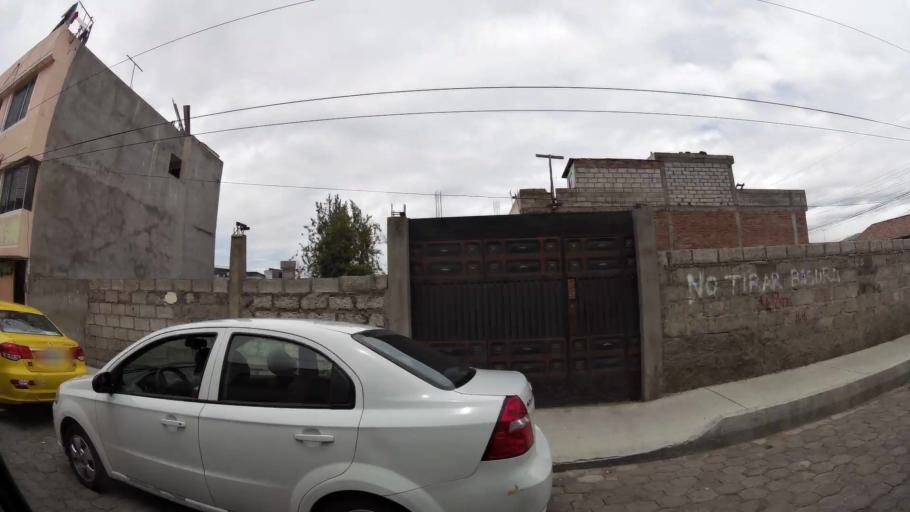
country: EC
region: Cotopaxi
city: San Miguel de Salcedo
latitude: -1.0463
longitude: -78.5896
